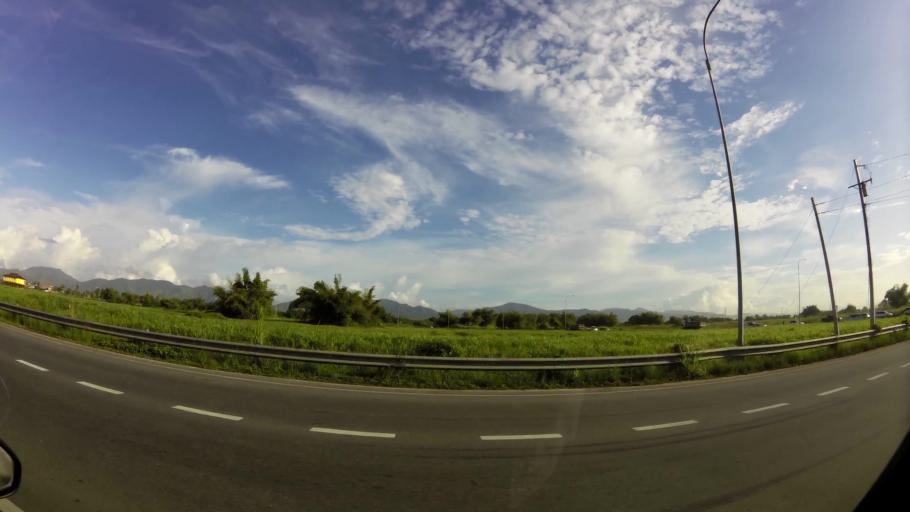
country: TT
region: Tunapuna/Piarco
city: Arouca
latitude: 10.5849
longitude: -61.3555
